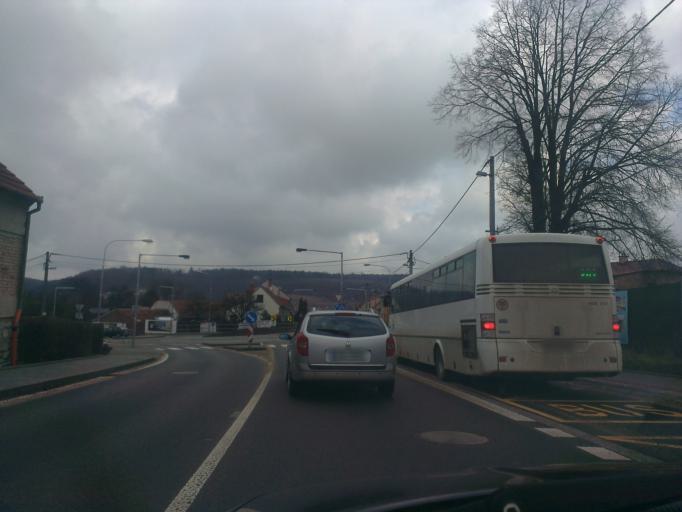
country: CZ
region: South Moravian
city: Bilovice nad Svitavou
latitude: 49.2507
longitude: 16.7336
